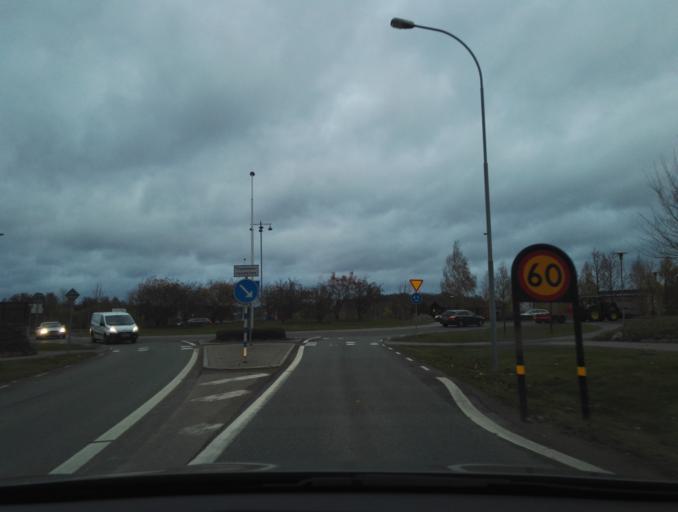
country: SE
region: Kronoberg
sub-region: Vaxjo Kommun
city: Vaexjoe
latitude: 56.8580
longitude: 14.8202
